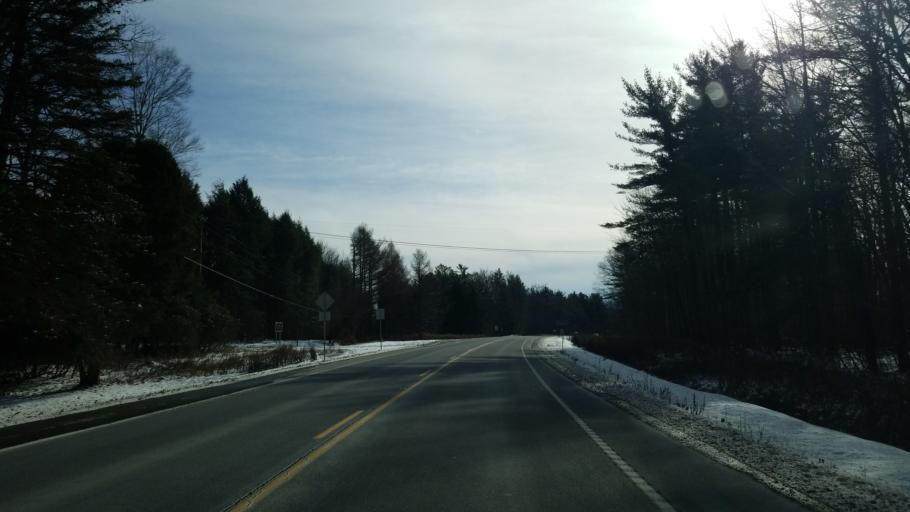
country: US
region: Pennsylvania
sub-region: Clearfield County
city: Clearfield
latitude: 41.1250
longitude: -78.5345
